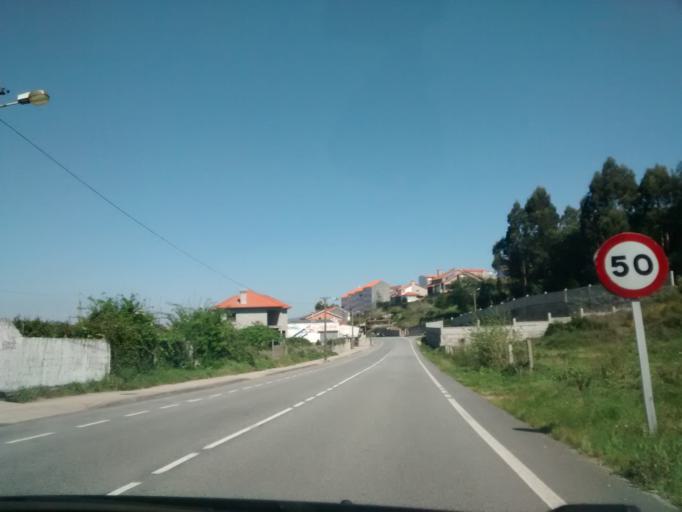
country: ES
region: Galicia
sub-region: Provincia de Pontevedra
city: O Grove
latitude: 42.4862
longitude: -8.8717
